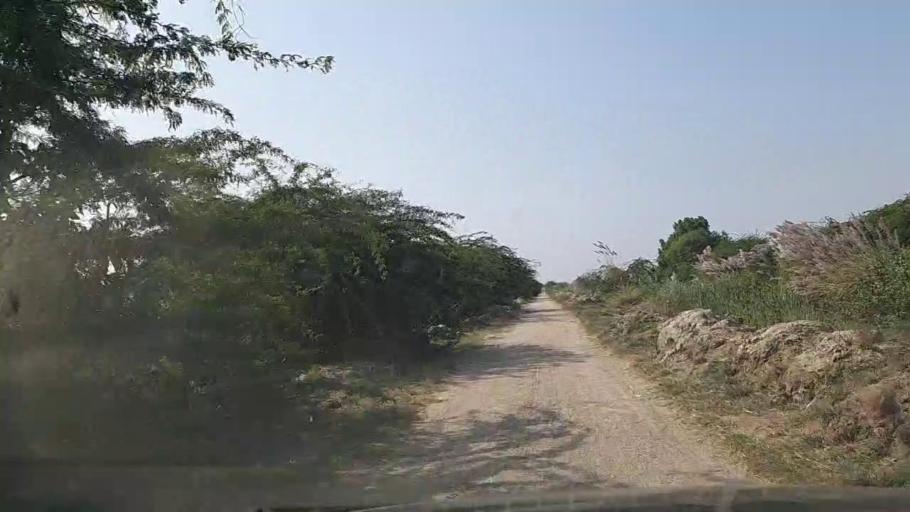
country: PK
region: Sindh
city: Gharo
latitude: 24.6979
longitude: 67.6219
